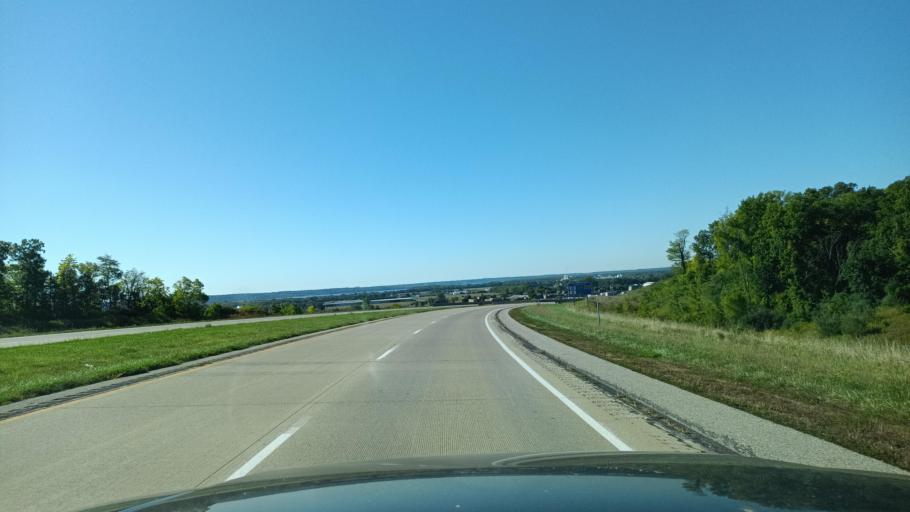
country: US
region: Iowa
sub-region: Lee County
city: Fort Madison
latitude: 40.6355
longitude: -91.3802
